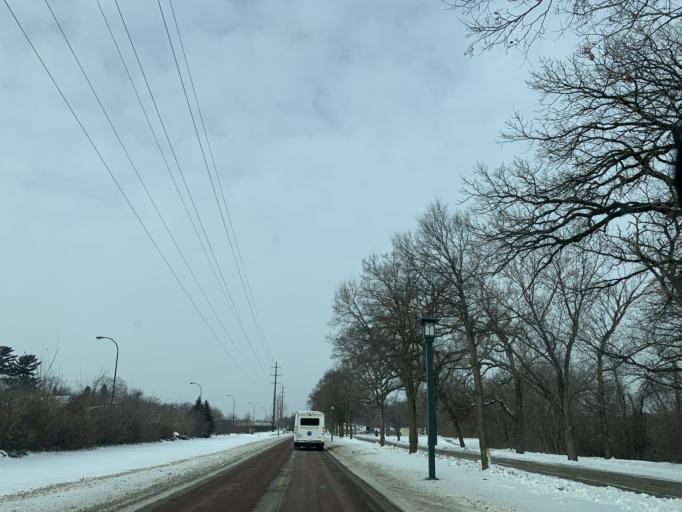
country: US
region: Minnesota
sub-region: Dakota County
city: Mendota Heights
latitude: 44.9102
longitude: -93.2066
